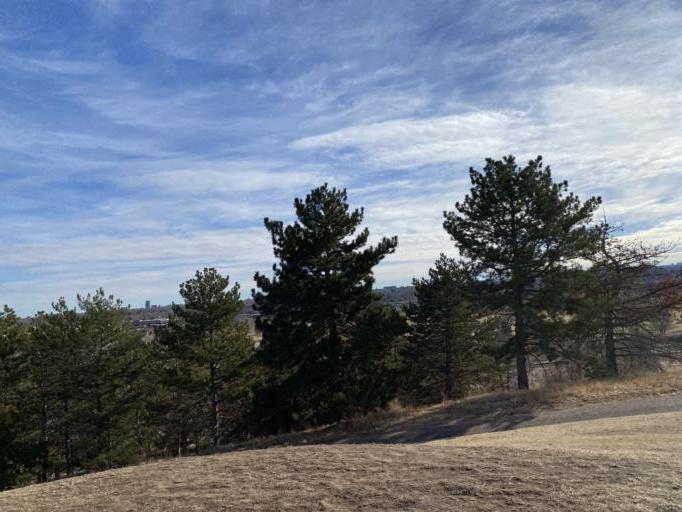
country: US
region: Colorado
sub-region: Arapahoe County
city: Englewood
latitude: 39.6886
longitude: -105.0030
